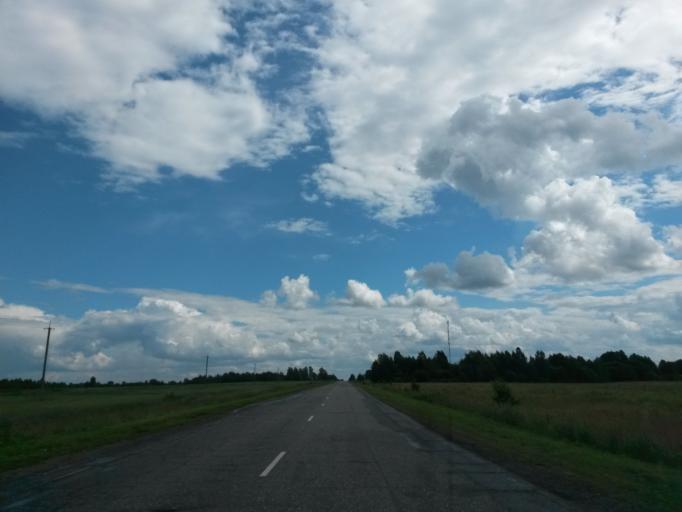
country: RU
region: Jaroslavl
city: Dubki
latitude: 57.2133
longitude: 40.2895
